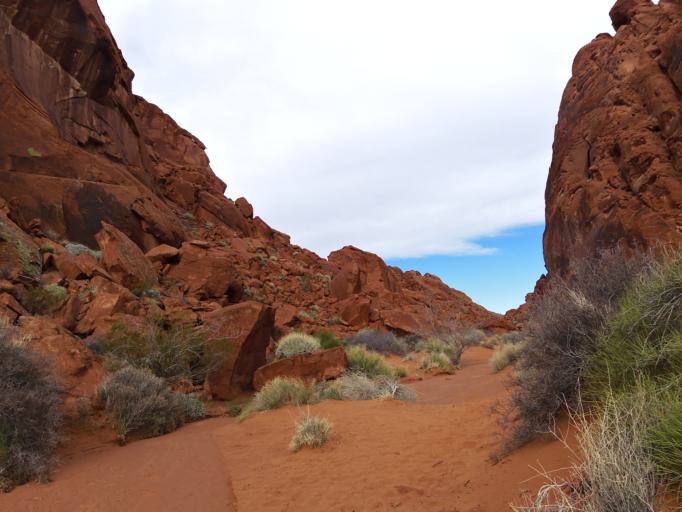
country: US
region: Nevada
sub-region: Clark County
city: Moapa Valley
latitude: 36.4471
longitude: -114.5090
